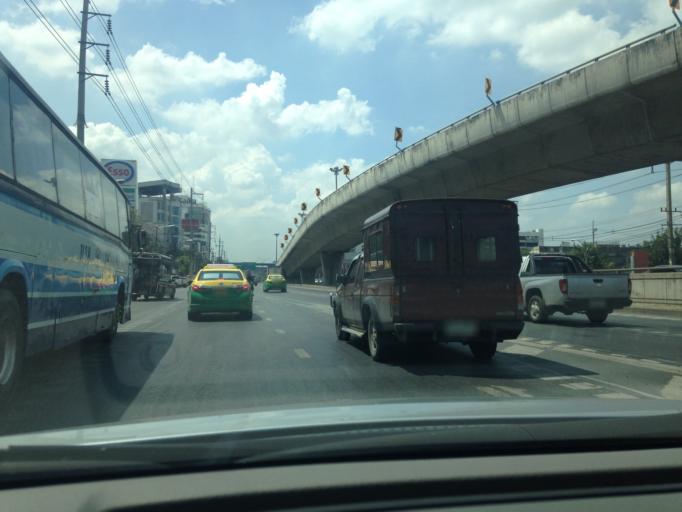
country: TH
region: Phra Nakhon Si Ayutthaya
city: Ban Bang Kadi Pathum Thani
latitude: 13.9879
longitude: 100.6136
